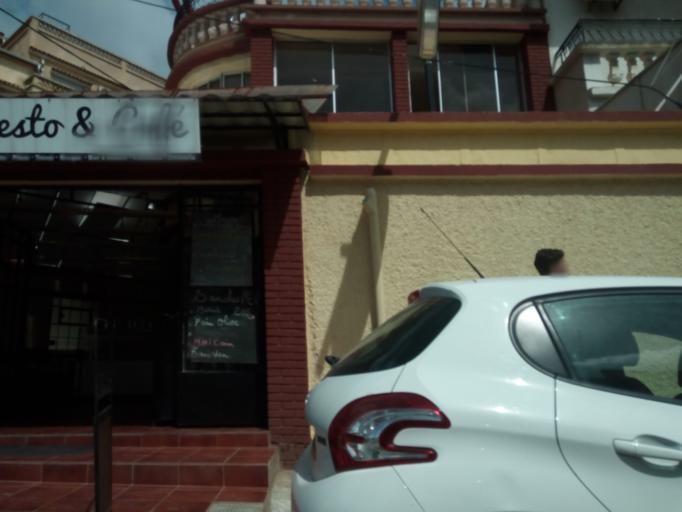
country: DZ
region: Tipaza
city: Douera
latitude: 36.6994
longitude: 2.9708
